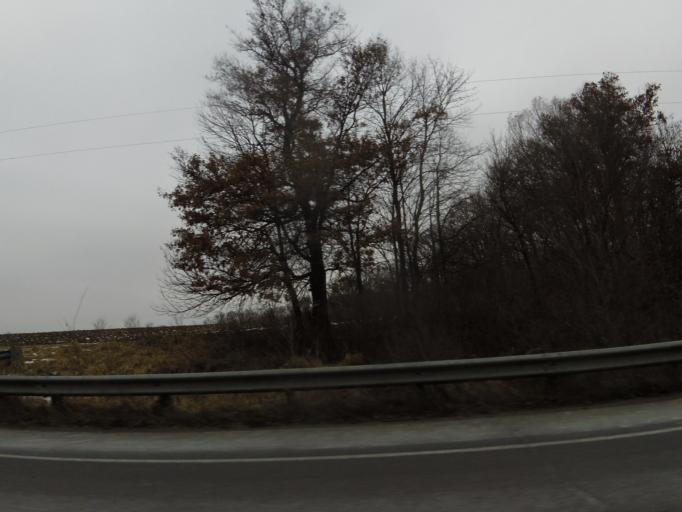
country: US
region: Minnesota
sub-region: Carver County
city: Cologne
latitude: 44.7758
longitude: -93.7290
